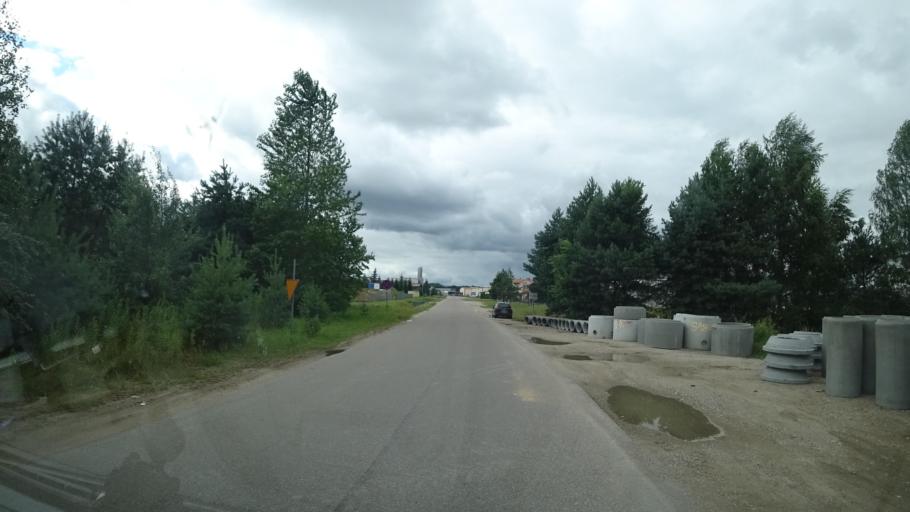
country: PL
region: Warmian-Masurian Voivodeship
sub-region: Powiat goldapski
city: Goldap
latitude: 54.3330
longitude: 22.2947
